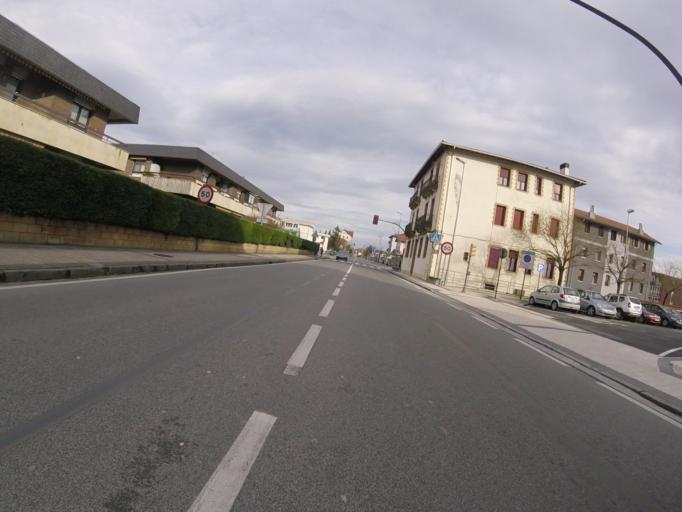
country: ES
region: Basque Country
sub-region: Provincia de Guipuzcoa
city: Irun
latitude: 43.3467
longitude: -1.8017
